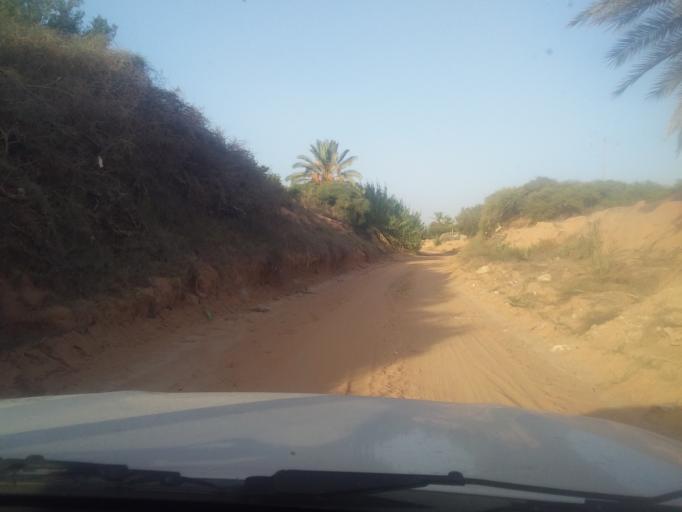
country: TN
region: Qabis
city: Gabes
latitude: 33.6302
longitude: 10.3000
